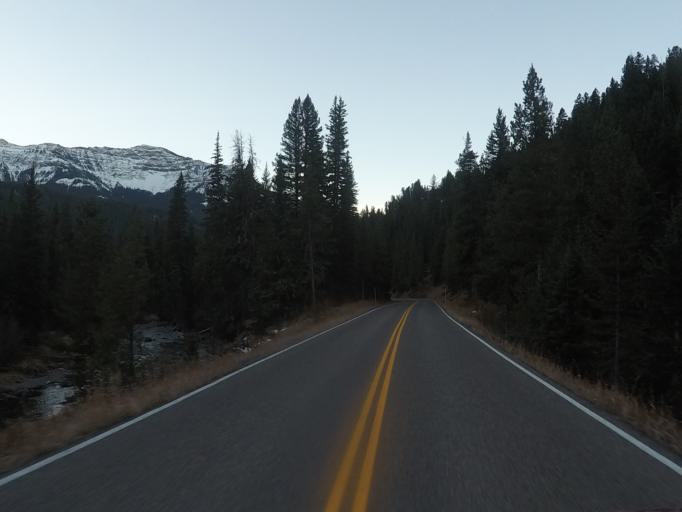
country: US
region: Montana
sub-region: Stillwater County
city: Absarokee
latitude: 44.9425
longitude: -110.0836
